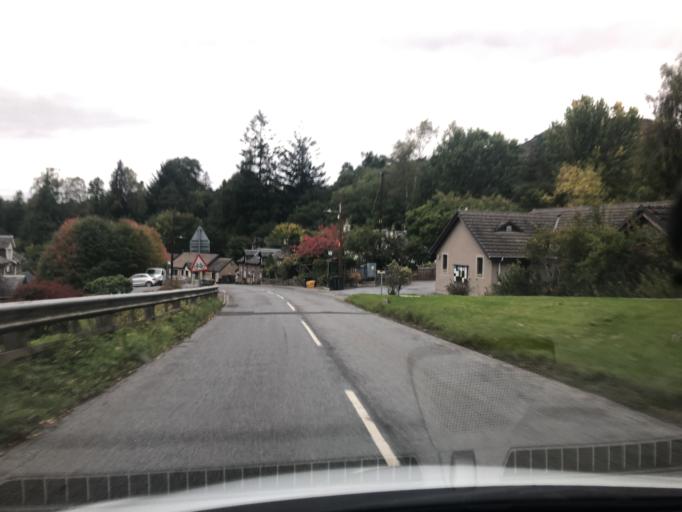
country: GB
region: Scotland
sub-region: Perth and Kinross
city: Pitlochry
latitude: 56.7442
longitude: -3.7781
